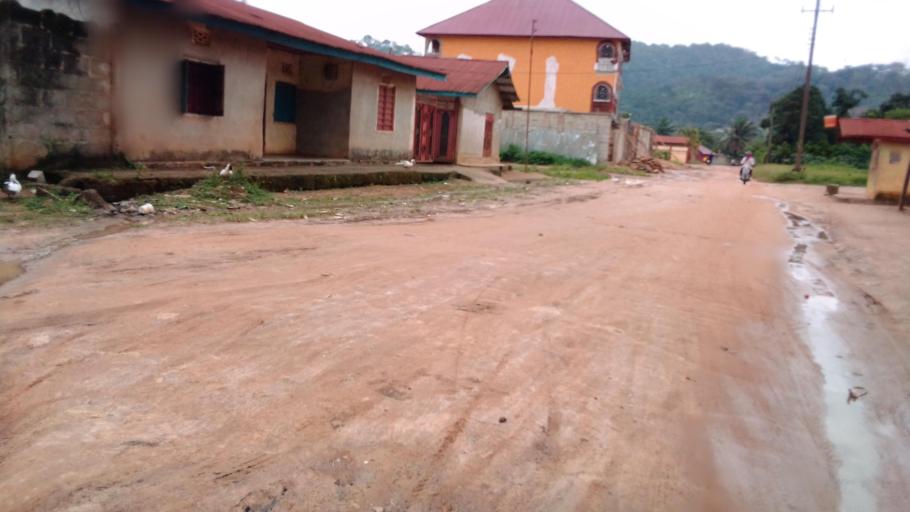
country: SL
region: Eastern Province
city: Kenema
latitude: 7.8697
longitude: -11.1991
